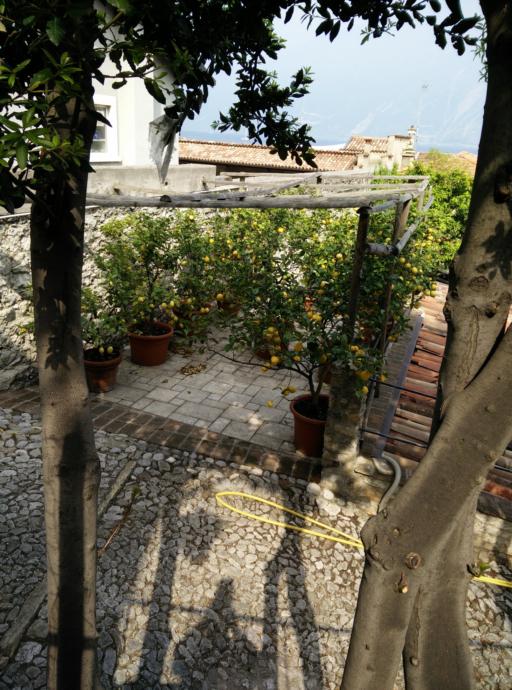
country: IT
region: Lombardy
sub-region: Provincia di Brescia
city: Limone sul Garda
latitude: 45.8145
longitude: 10.7928
